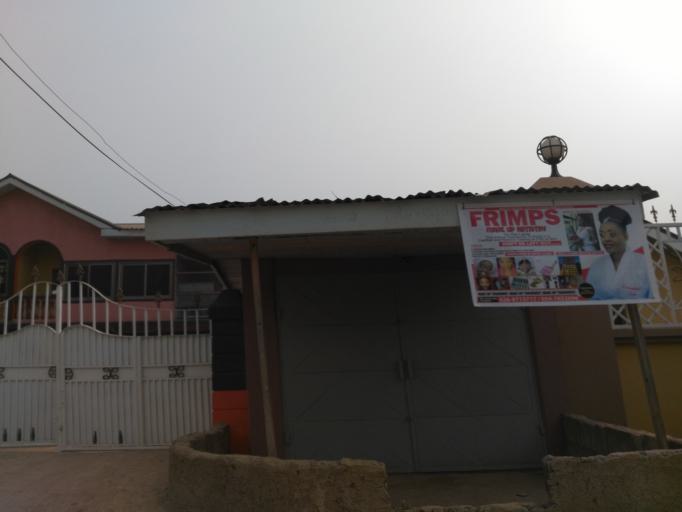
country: GH
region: Ashanti
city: Kumasi
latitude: 6.6550
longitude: -1.6255
